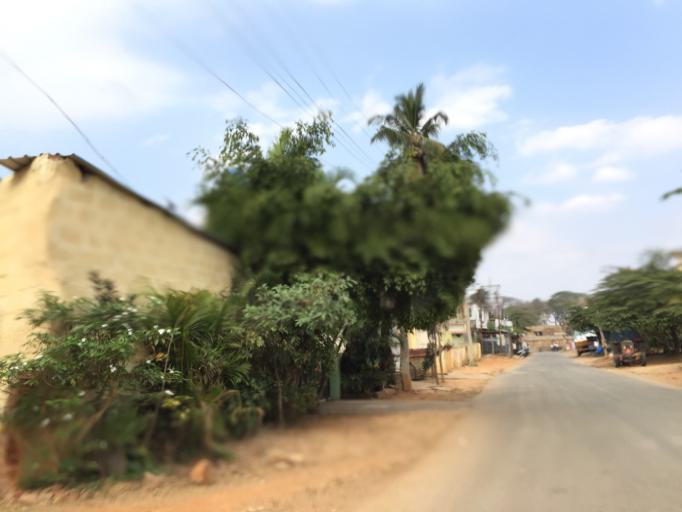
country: IN
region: Karnataka
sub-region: Chikkaballapur
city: Chik Ballapur
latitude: 13.3857
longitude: 77.6966
